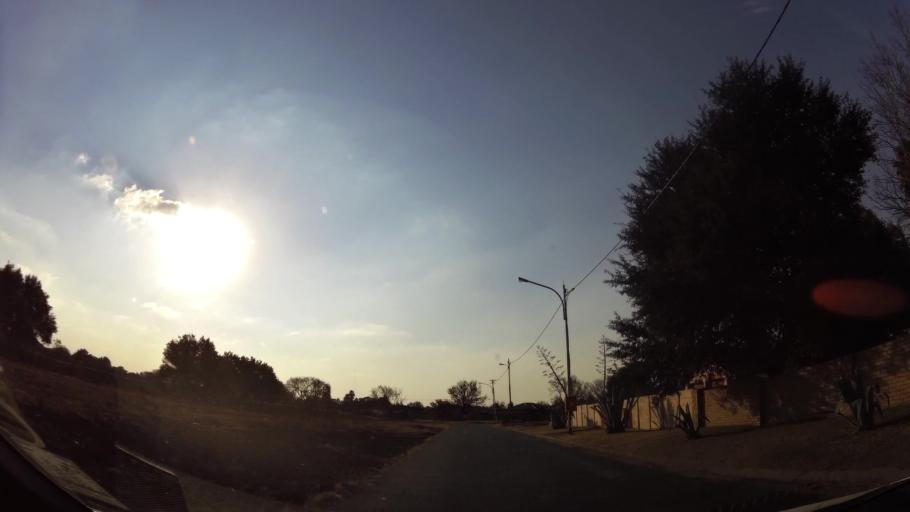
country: ZA
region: Gauteng
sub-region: Ekurhuleni Metropolitan Municipality
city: Springs
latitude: -26.2593
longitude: 28.3869
